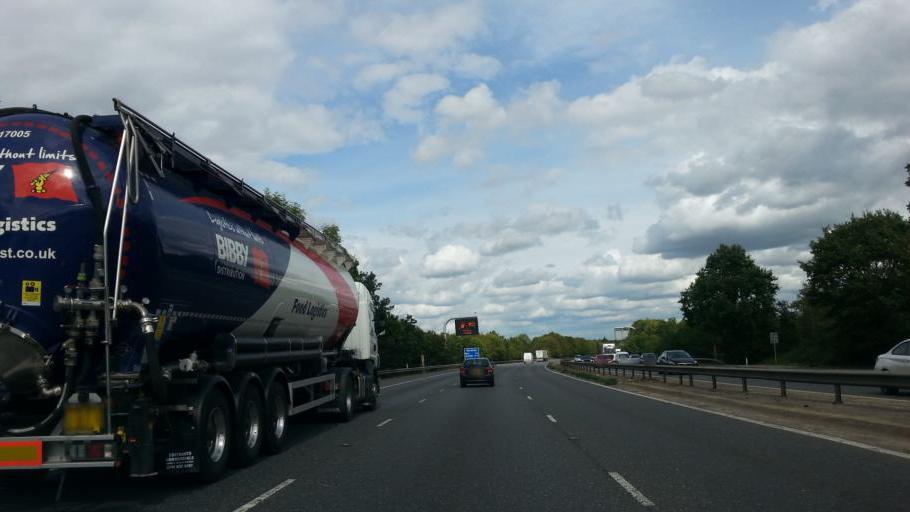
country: GB
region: England
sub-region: Essex
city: Little Hallingbury
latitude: 51.8243
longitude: 0.1859
